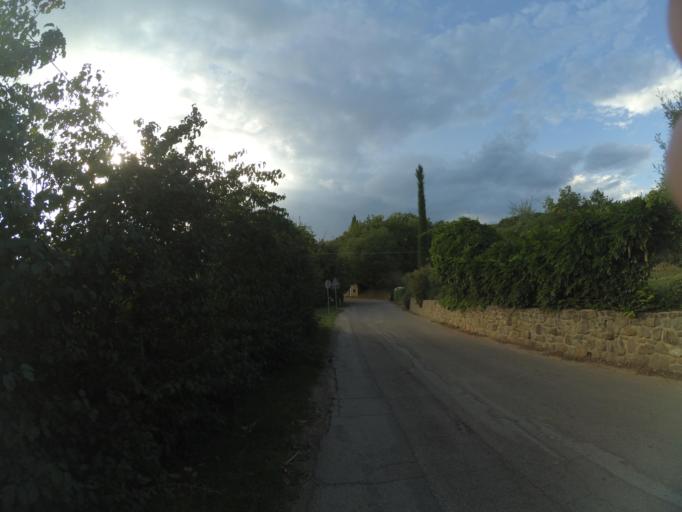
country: IT
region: Tuscany
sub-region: Province of Arezzo
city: Castiglion Fibocchi
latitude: 43.5301
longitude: 11.7711
